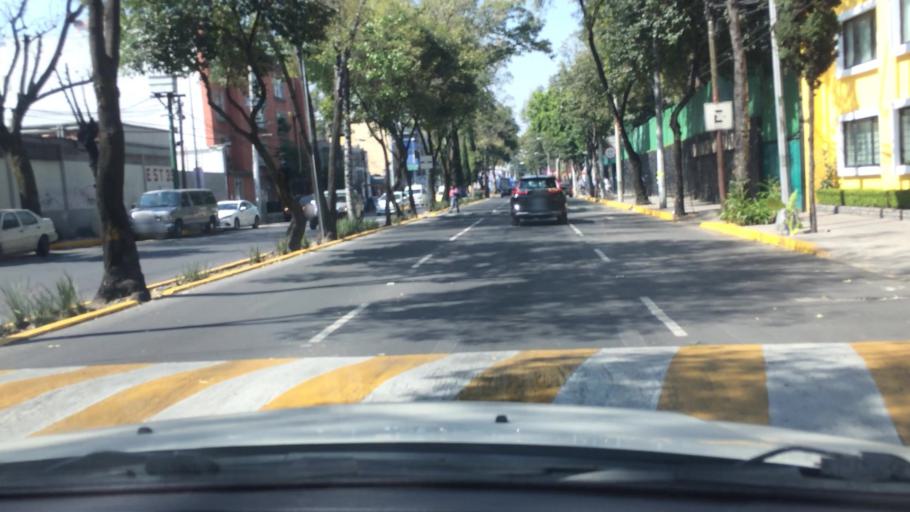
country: MX
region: Mexico City
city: Tlalpan
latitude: 19.2945
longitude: -99.1737
